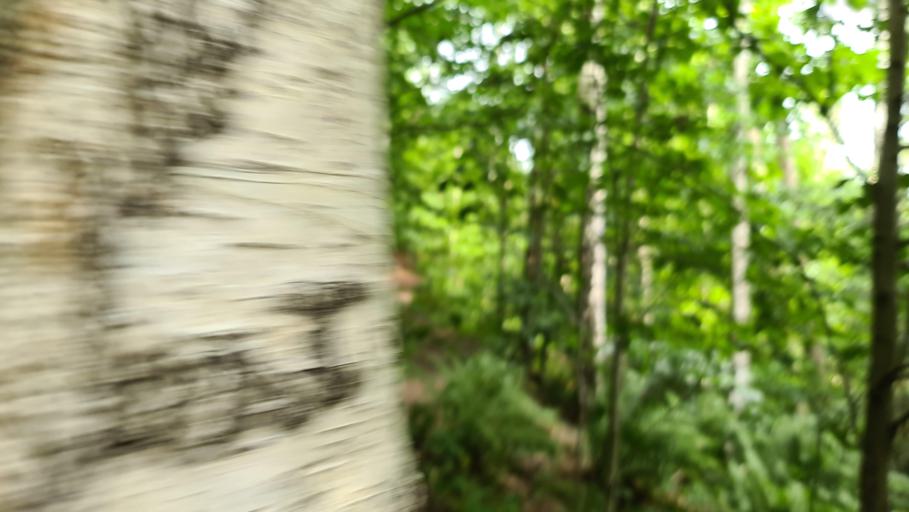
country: DE
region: Saxony
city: Oelsnitz
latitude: 50.7264
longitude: 12.6861
